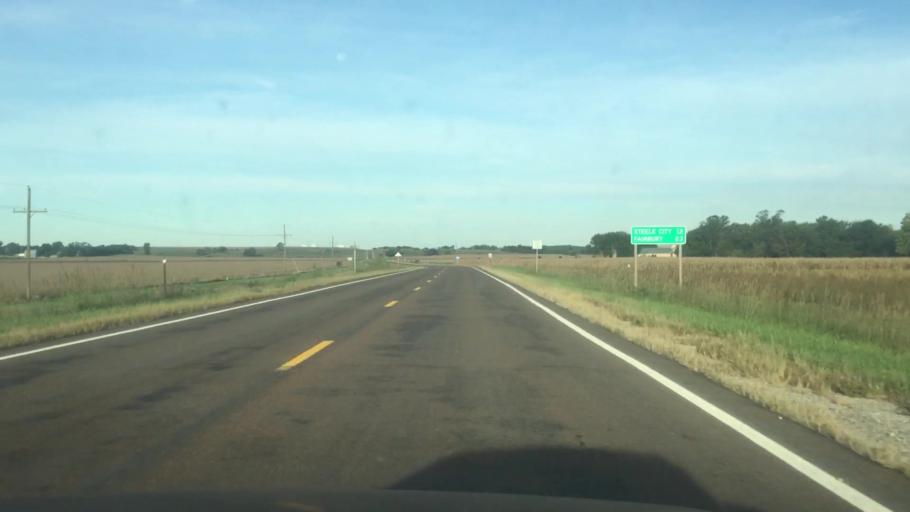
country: US
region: Nebraska
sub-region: Gage County
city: Wymore
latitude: 40.0455
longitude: -96.8060
